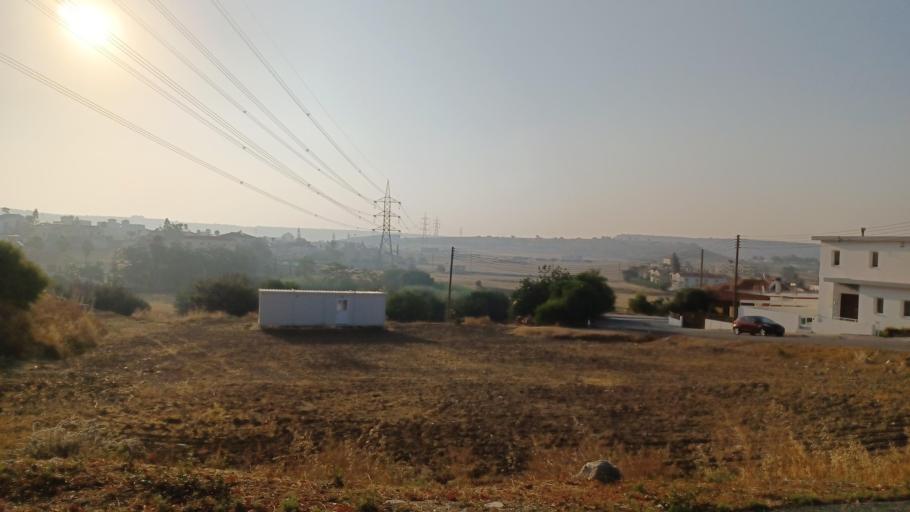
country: CY
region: Larnaka
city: Pyla
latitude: 35.0042
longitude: 33.6847
